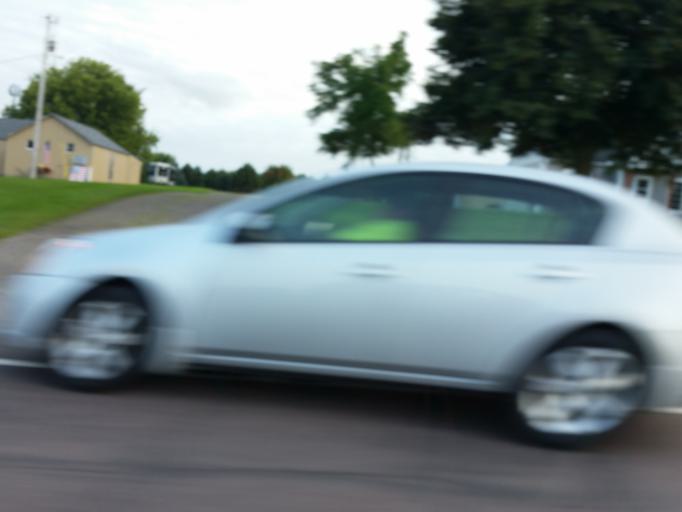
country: US
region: Minnesota
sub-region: Dakota County
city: Farmington
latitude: 44.6305
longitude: -93.0926
